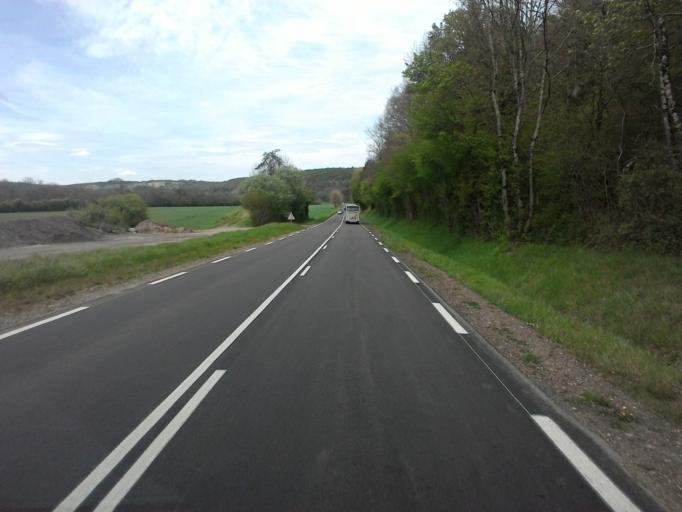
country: FR
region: Bourgogne
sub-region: Departement de l'Yonne
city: Joux-la-Ville
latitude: 47.5654
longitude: 3.7809
